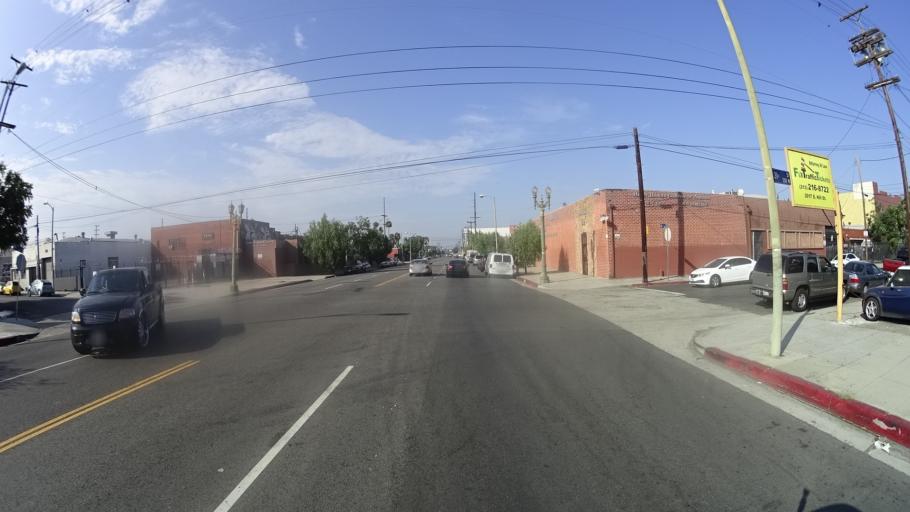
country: US
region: California
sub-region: Los Angeles County
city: Los Angeles
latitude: 34.0222
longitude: -118.2733
